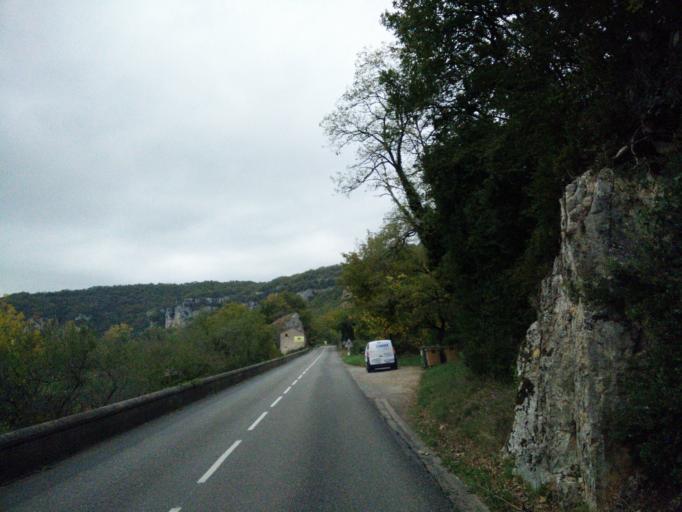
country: FR
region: Midi-Pyrenees
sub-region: Departement du Lot
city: Cahors
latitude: 44.4769
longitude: 1.5652
